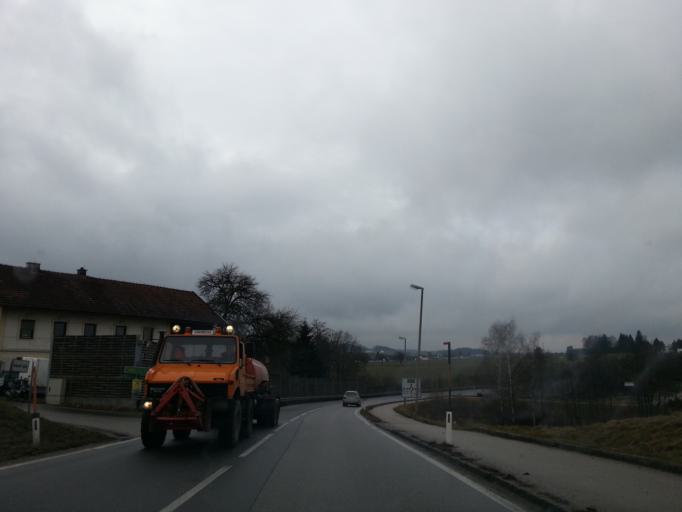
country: AT
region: Upper Austria
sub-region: Politischer Bezirk Ried im Innkreis
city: Ried im Innkreis
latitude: 48.2054
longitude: 13.4698
